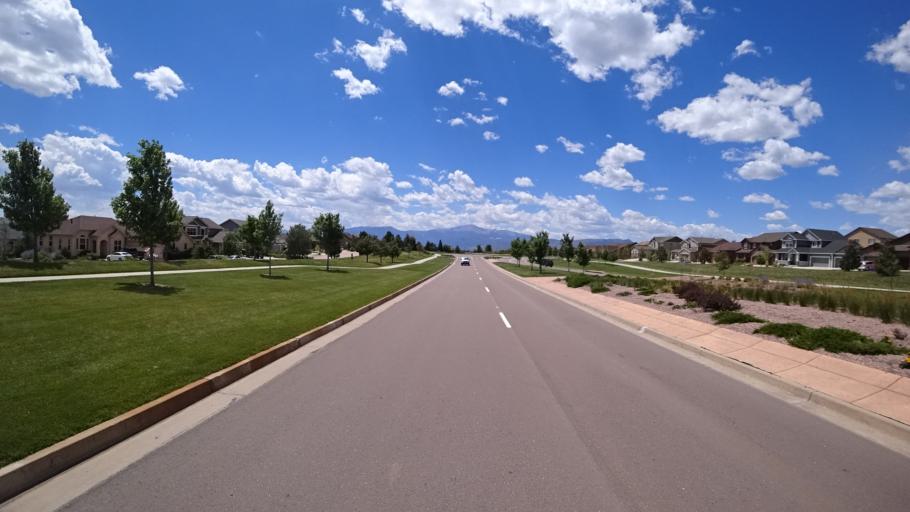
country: US
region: Colorado
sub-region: El Paso County
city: Black Forest
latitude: 38.9618
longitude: -104.7163
